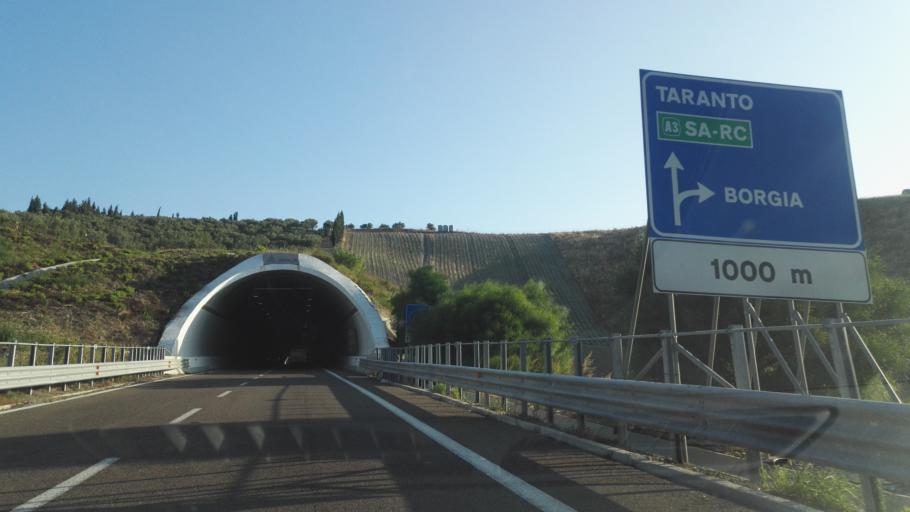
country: IT
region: Calabria
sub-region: Provincia di Catanzaro
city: Squillace Lido
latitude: 38.8114
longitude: 16.5586
